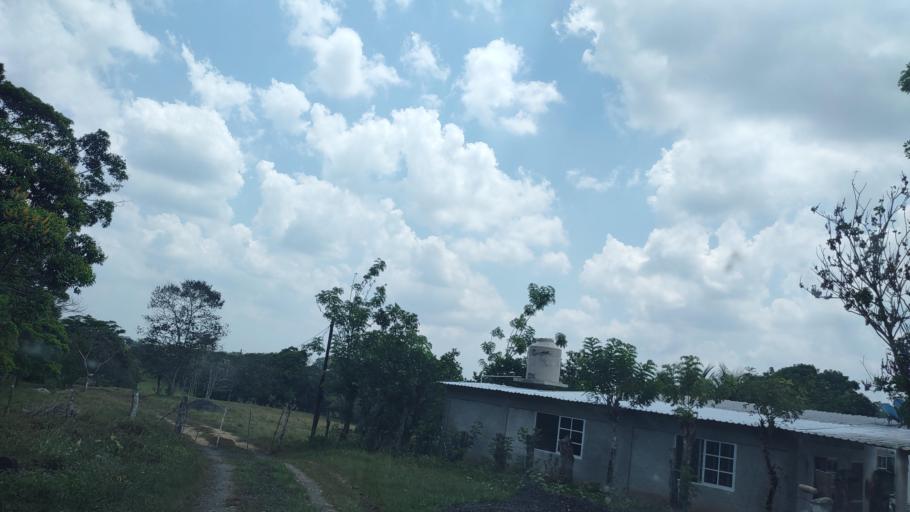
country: MX
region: Veracruz
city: Las Choapas
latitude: 17.9338
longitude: -94.1497
